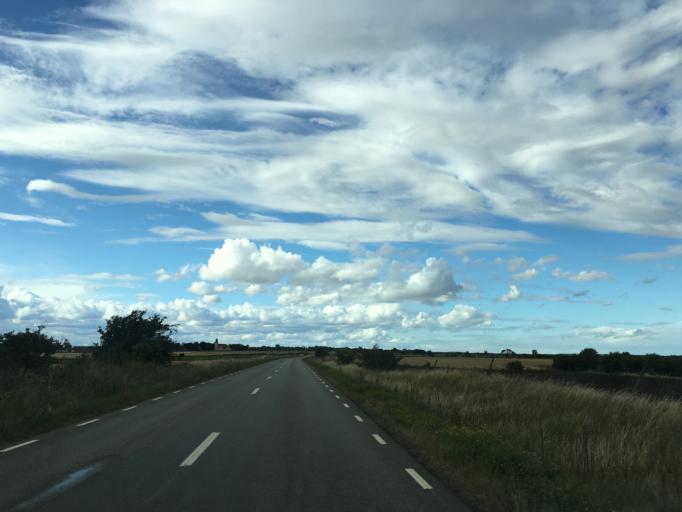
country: SE
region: Kalmar
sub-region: Morbylanga Kommun
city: Moerbylanga
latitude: 56.3951
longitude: 16.4368
